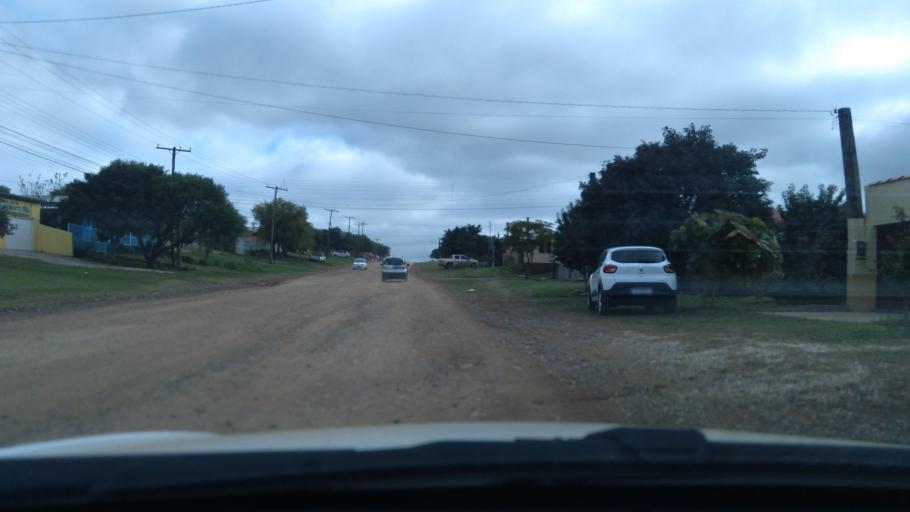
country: BR
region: Rio Grande do Sul
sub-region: Dom Pedrito
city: Dom Pedrito
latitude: -30.9814
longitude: -54.6549
